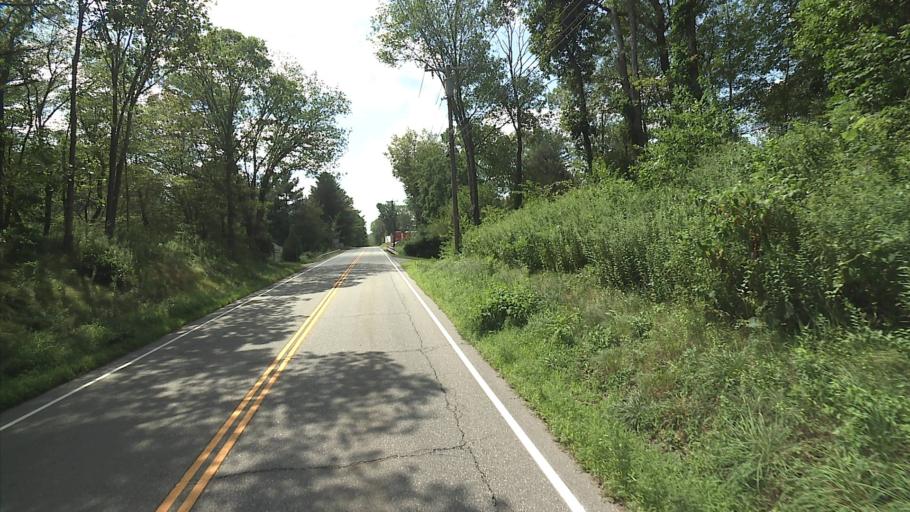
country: US
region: Connecticut
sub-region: Windham County
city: South Woodstock
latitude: 41.8750
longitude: -72.0874
